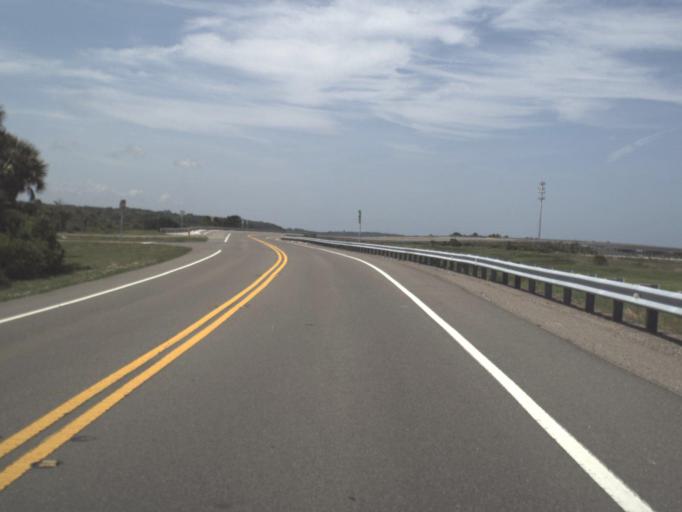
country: US
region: Florida
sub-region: Duval County
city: Atlantic Beach
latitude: 30.4128
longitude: -81.4219
